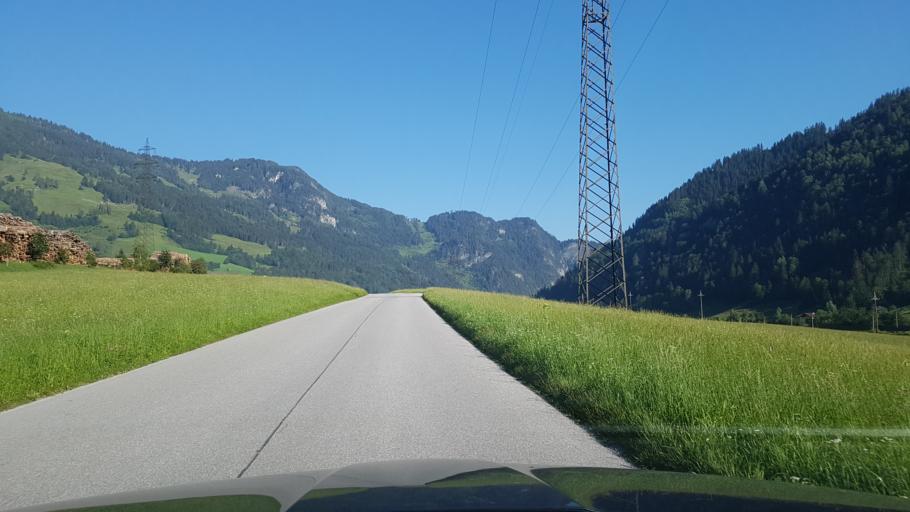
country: AT
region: Salzburg
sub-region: Politischer Bezirk Sankt Johann im Pongau
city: Dorfgastein
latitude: 47.2514
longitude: 13.0948
